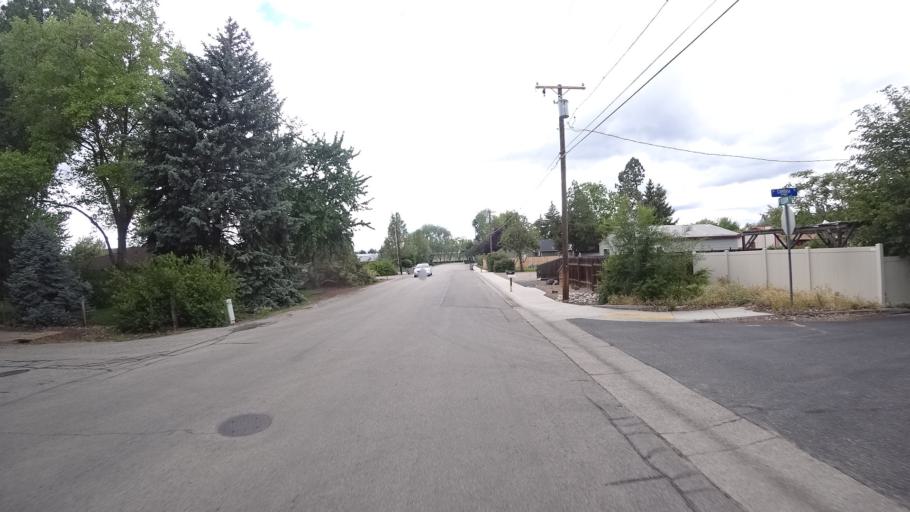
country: US
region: Idaho
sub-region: Ada County
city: Garden City
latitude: 43.6575
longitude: -116.2550
